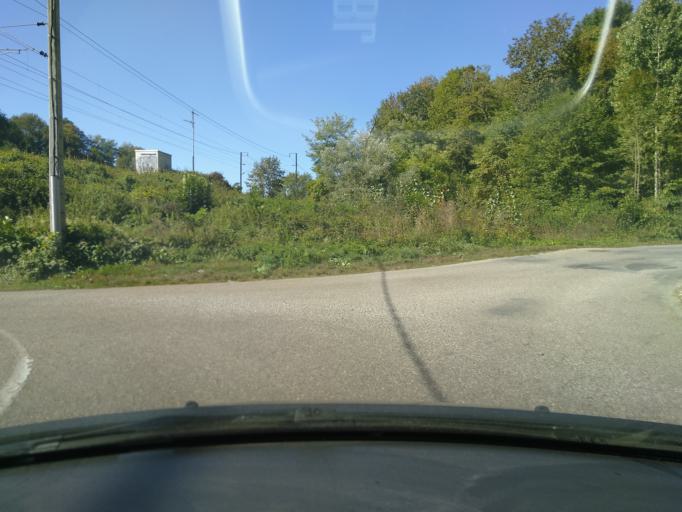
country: FR
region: Rhone-Alpes
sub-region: Departement de l'Isere
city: La Murette
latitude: 45.3690
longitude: 5.5346
